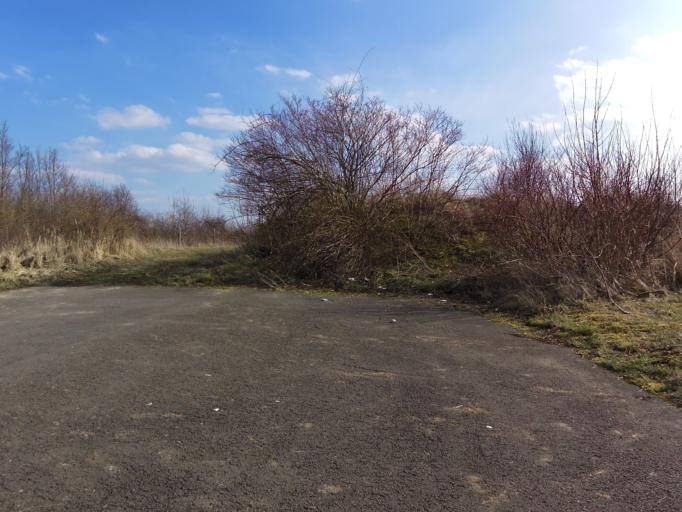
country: DE
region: Saxony
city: Markranstadt
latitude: 51.3011
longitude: 12.2724
